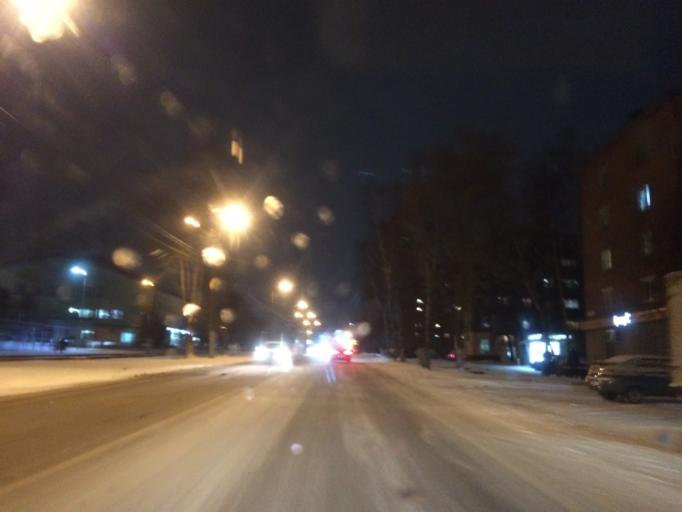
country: RU
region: Tula
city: Tula
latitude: 54.2142
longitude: 37.6688
